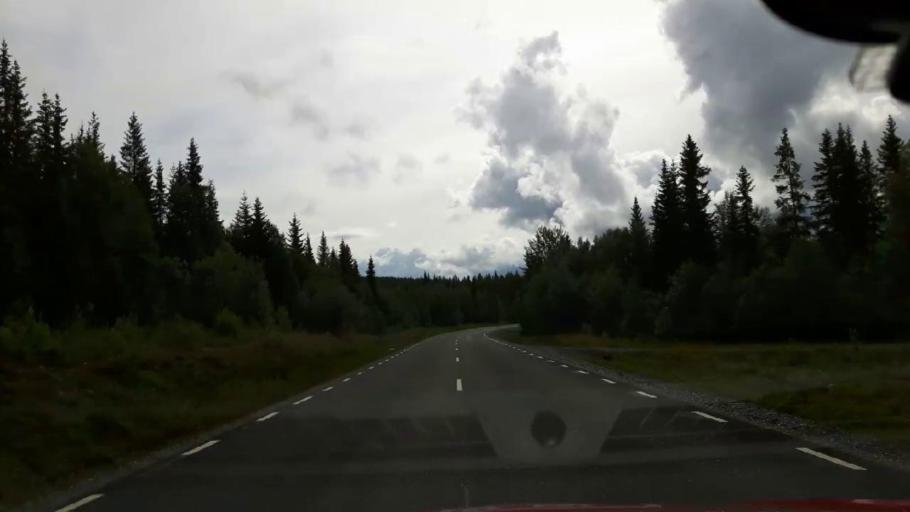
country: NO
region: Nord-Trondelag
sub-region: Lierne
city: Sandvika
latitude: 64.6186
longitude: 14.1226
